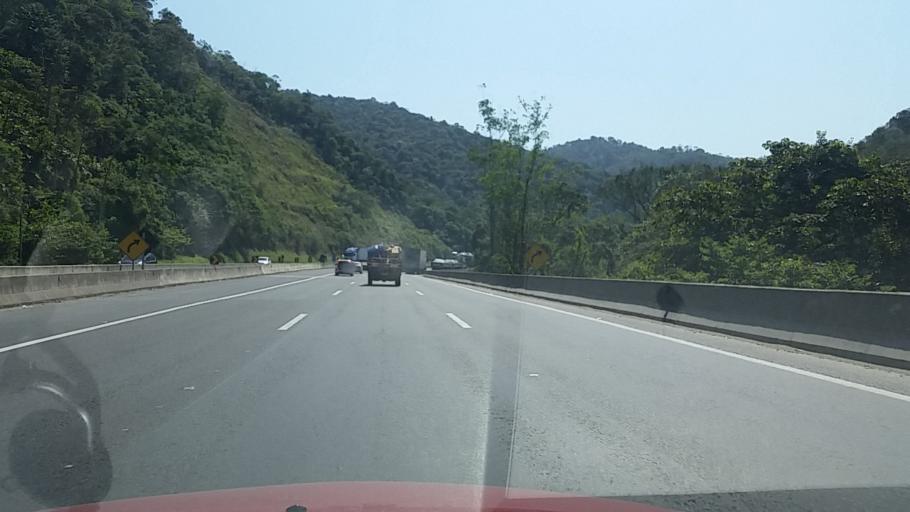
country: BR
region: Sao Paulo
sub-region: Juquitiba
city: Juquitiba
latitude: -24.0922
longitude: -47.2561
